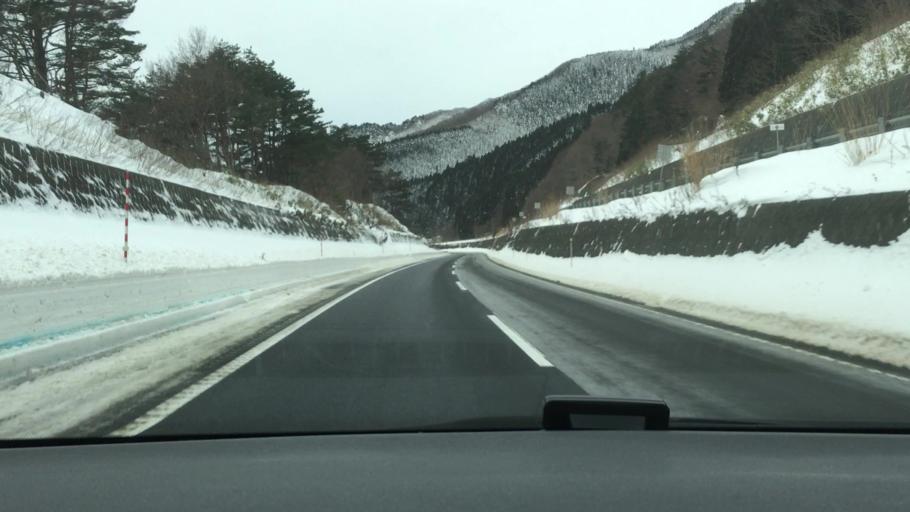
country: JP
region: Akita
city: Hanawa
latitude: 40.1222
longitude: 140.8425
